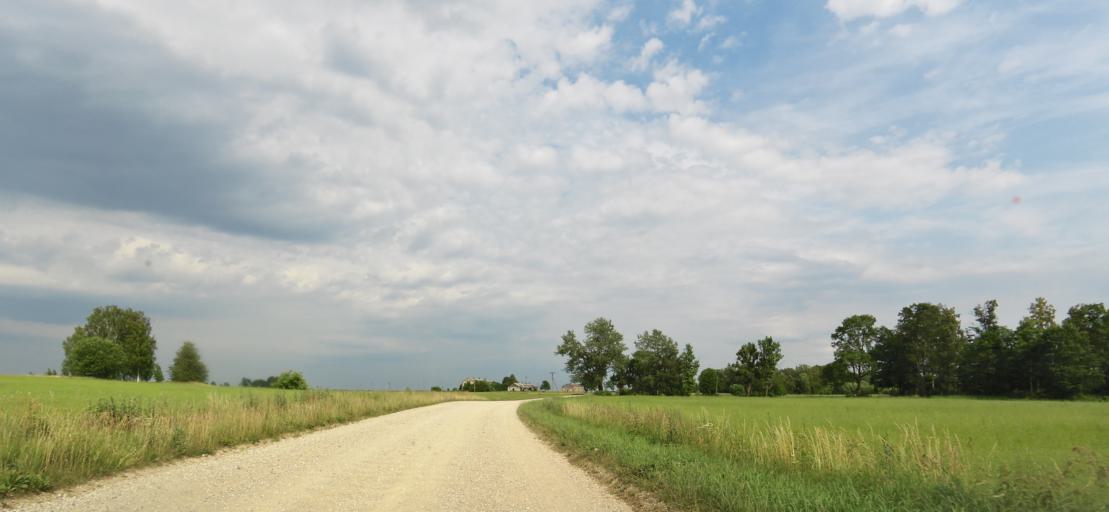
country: LT
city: Obeliai
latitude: 56.1529
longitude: 25.0333
